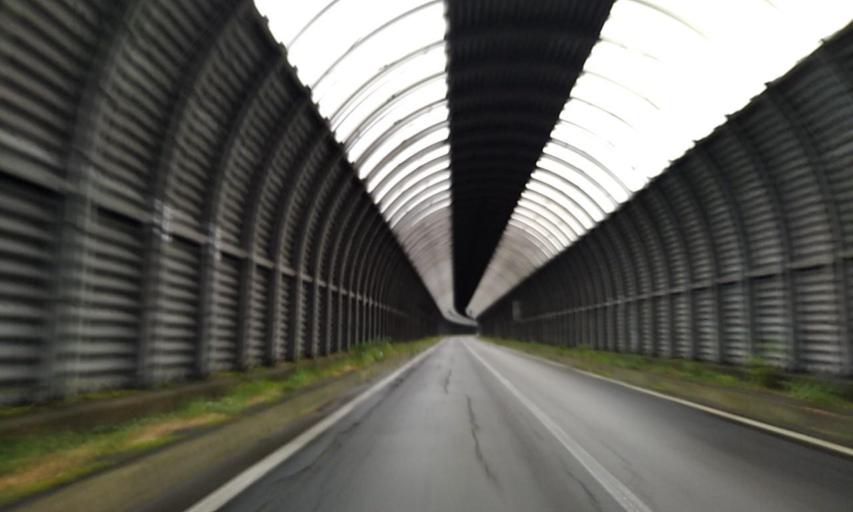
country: JP
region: Hokkaido
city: Abashiri
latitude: 43.6122
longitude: 144.5962
